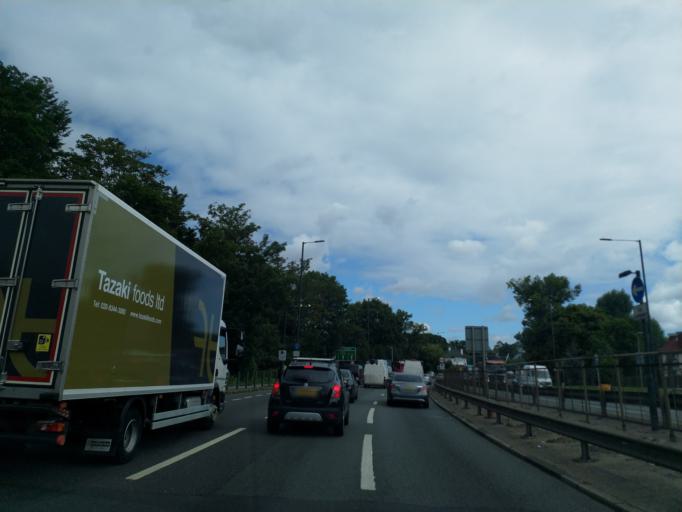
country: GB
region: England
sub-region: Greater London
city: Hendon
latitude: 51.5864
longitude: -0.2090
